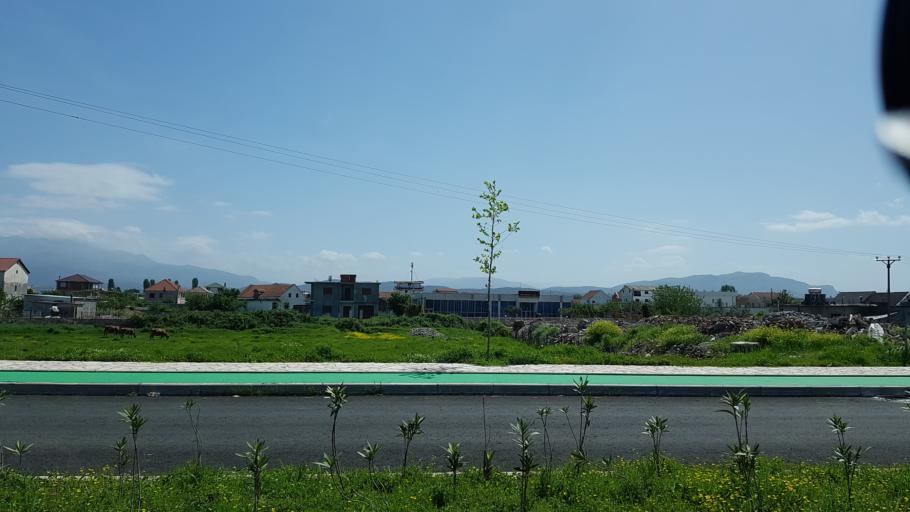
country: AL
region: Shkoder
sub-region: Rrethi i Shkodres
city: Shkoder
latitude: 42.0799
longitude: 19.4922
